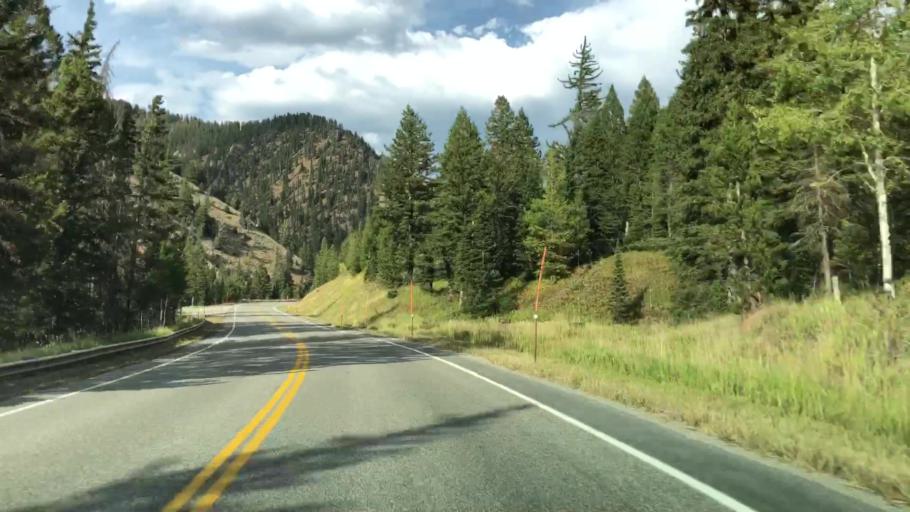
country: US
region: Wyoming
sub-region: Teton County
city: Hoback
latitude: 43.2825
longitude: -110.5746
